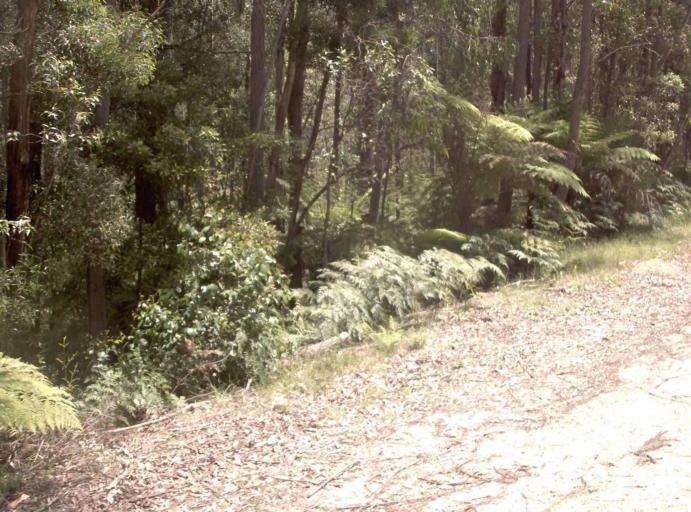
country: AU
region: New South Wales
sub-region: Bombala
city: Bombala
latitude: -37.5820
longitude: 148.9431
